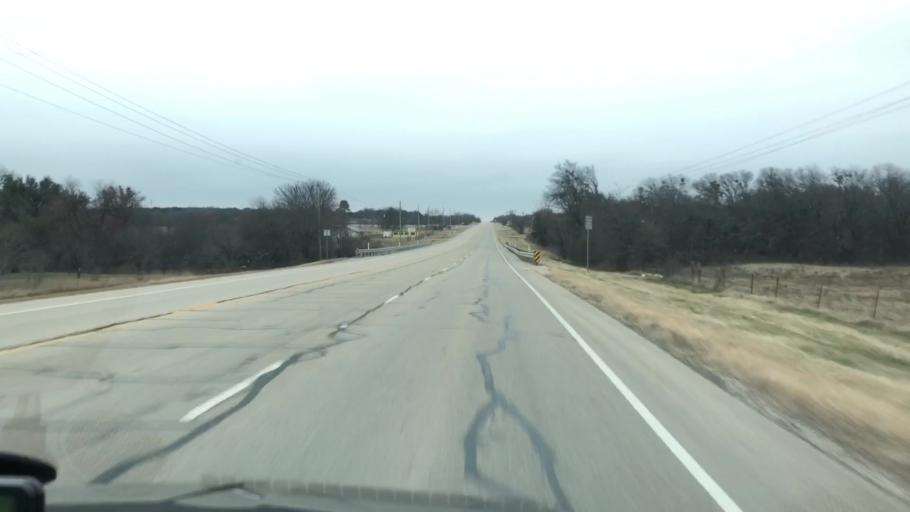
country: US
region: Texas
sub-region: Hamilton County
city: Hamilton
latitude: 31.7294
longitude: -98.1183
